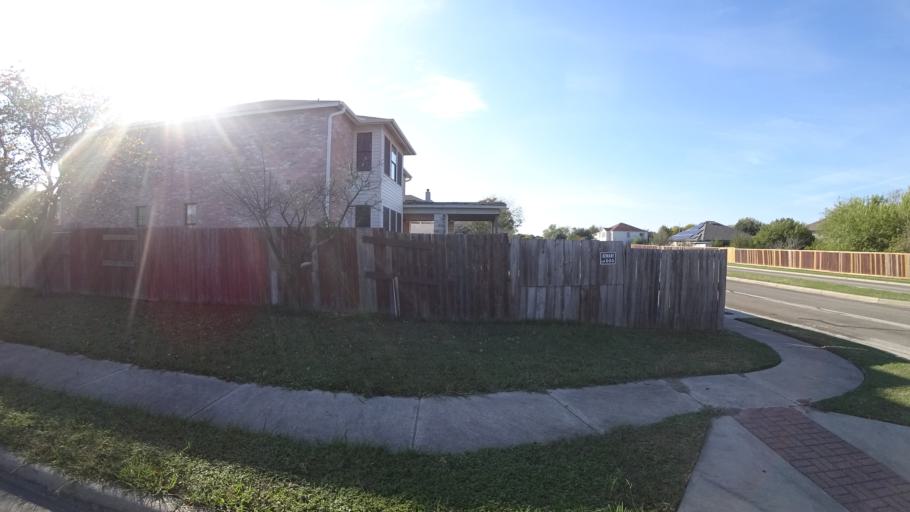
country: US
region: Texas
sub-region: Travis County
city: Pflugerville
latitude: 30.4030
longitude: -97.6516
